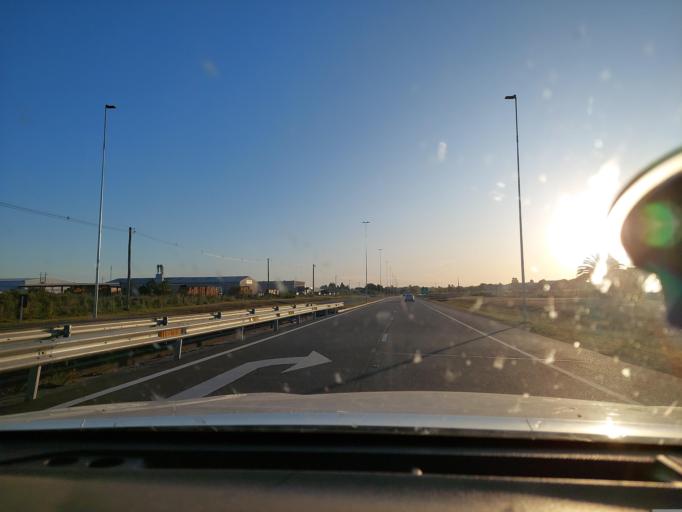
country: UY
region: Canelones
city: Pando
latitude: -34.7265
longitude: -55.9508
